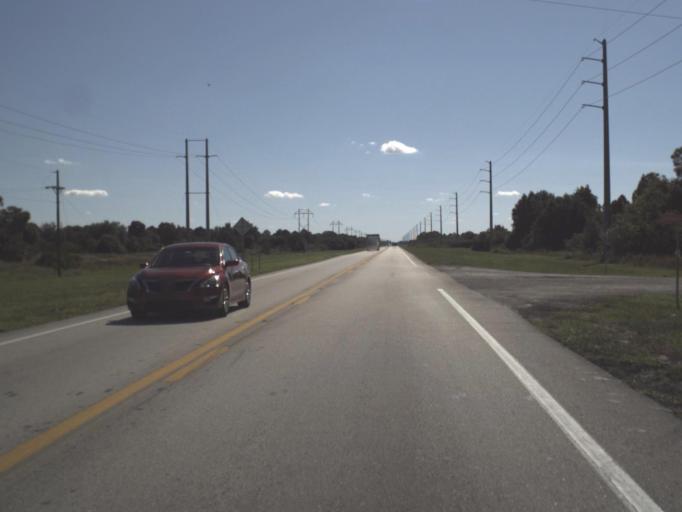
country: US
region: Florida
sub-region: Lee County
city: Gateway
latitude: 26.5795
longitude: -81.7085
